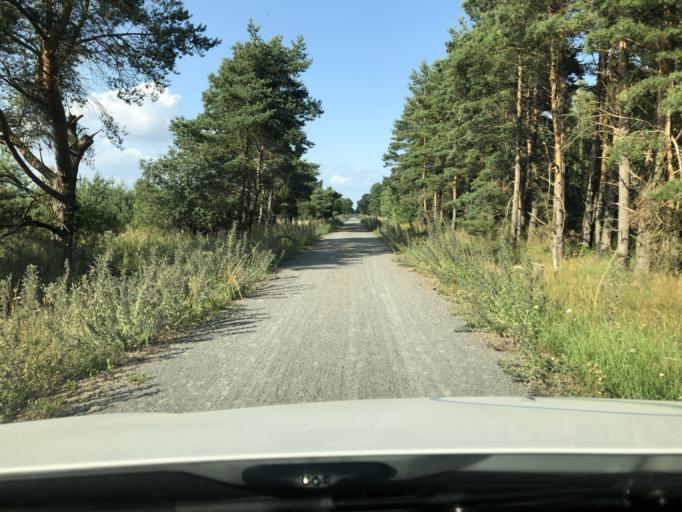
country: SE
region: Skane
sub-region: Kristianstads Kommun
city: Norra Asum
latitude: 55.9354
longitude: 14.1379
